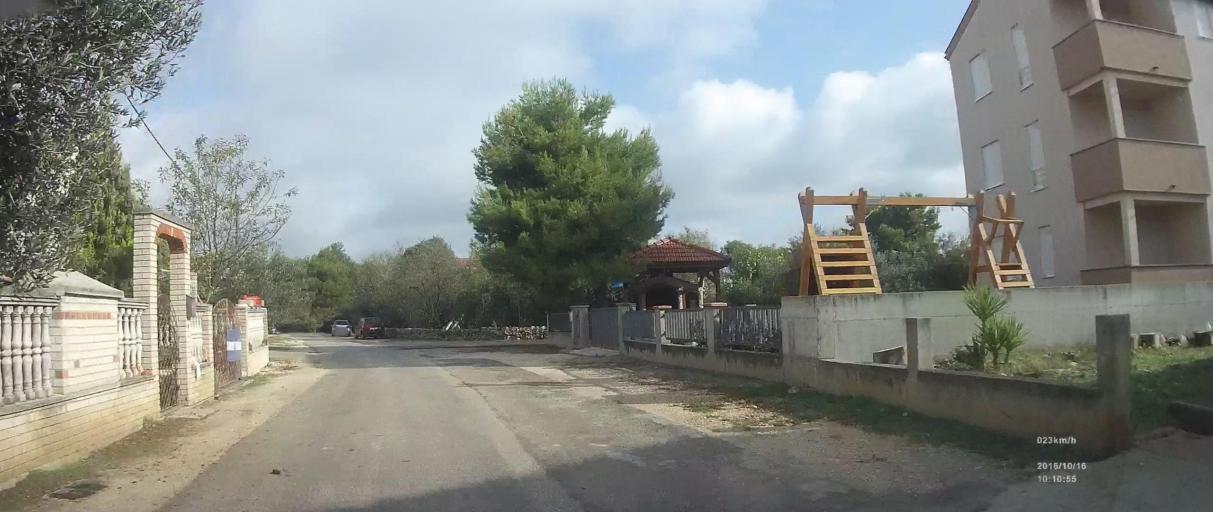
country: HR
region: Zadarska
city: Pakostane
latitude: 43.9139
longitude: 15.5071
